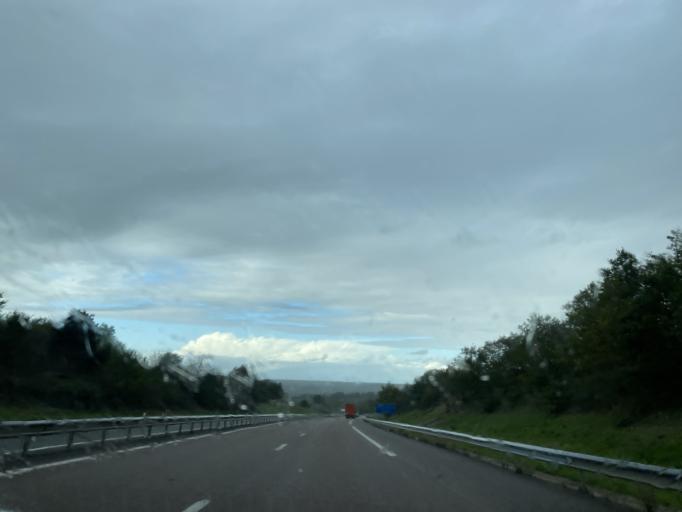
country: FR
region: Auvergne
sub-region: Departement de l'Allier
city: Vallon-en-Sully
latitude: 46.5021
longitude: 2.6442
